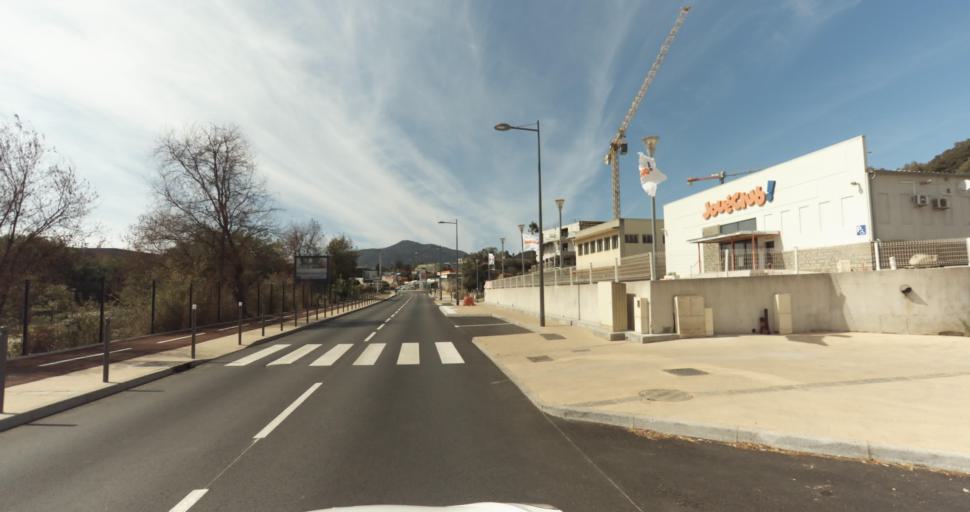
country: FR
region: Corsica
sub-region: Departement de la Corse-du-Sud
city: Afa
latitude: 41.9520
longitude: 8.7765
